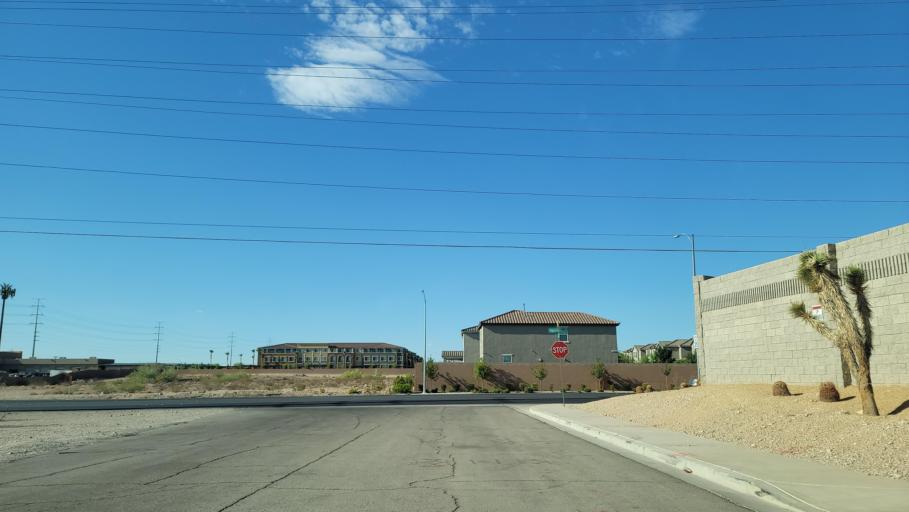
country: US
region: Nevada
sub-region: Clark County
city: Spring Valley
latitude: 36.0857
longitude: -115.2816
